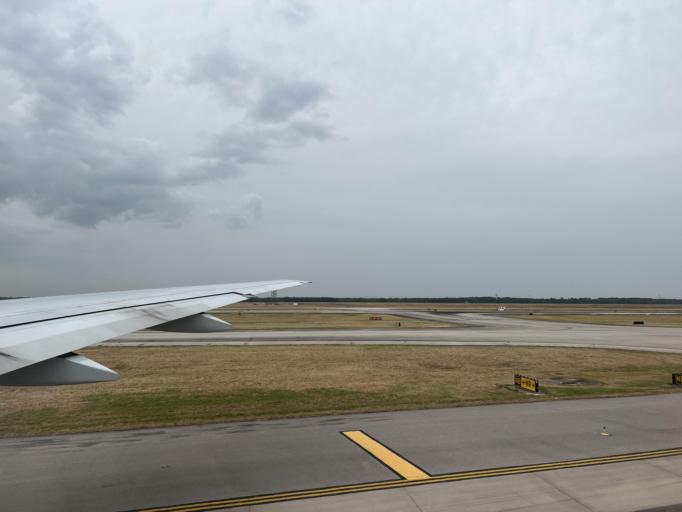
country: US
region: Texas
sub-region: Harris County
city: Aldine
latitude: 29.9908
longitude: -95.3536
